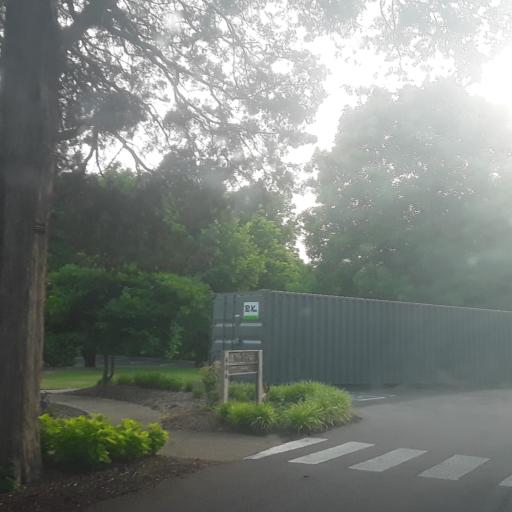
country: US
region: Tennessee
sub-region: Davidson County
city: Oak Hill
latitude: 36.0635
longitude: -86.7460
